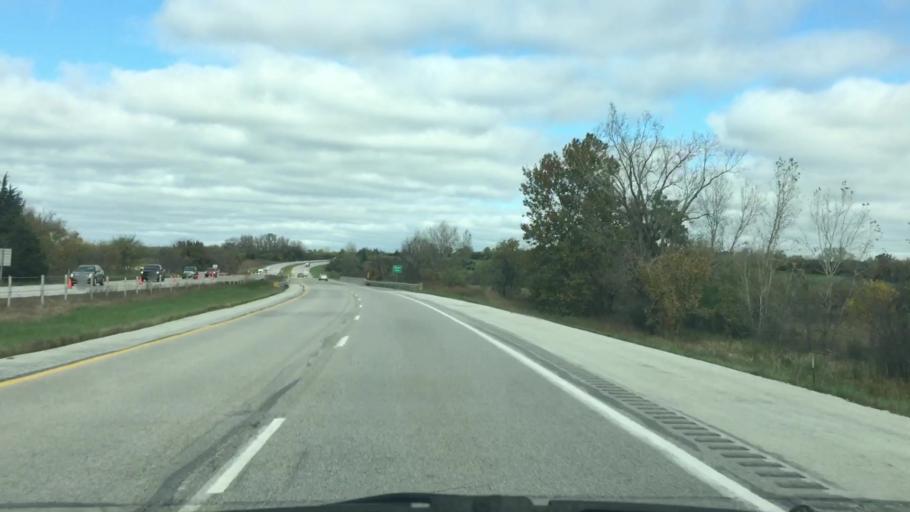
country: US
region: Iowa
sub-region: Clarke County
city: Osceola
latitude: 41.1040
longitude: -93.7775
